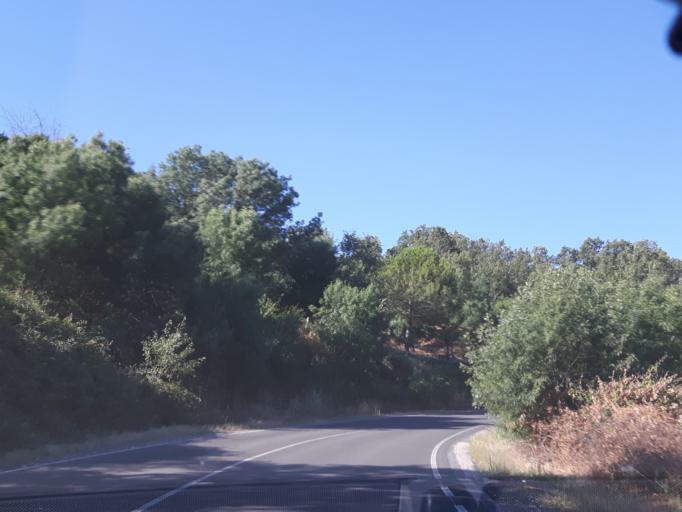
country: ES
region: Castille and Leon
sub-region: Provincia de Salamanca
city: Navalmoral de Bejar
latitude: 40.4125
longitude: -5.8030
